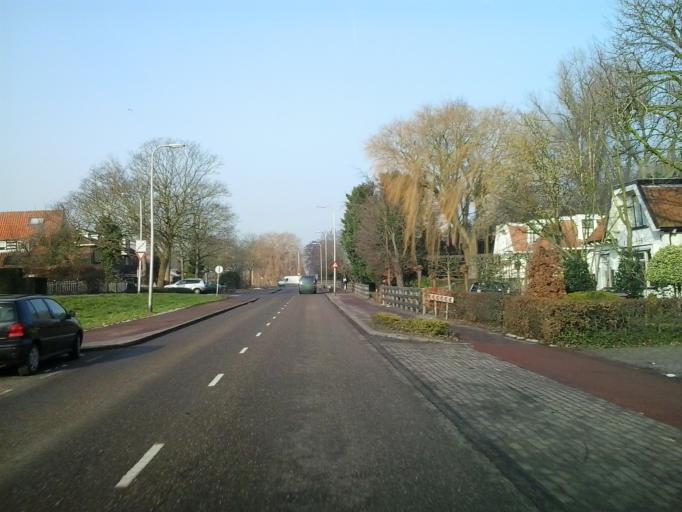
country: NL
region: South Holland
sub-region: Gemeente Zwijndrecht
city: Heerjansdam
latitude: 51.8562
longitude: 4.5814
